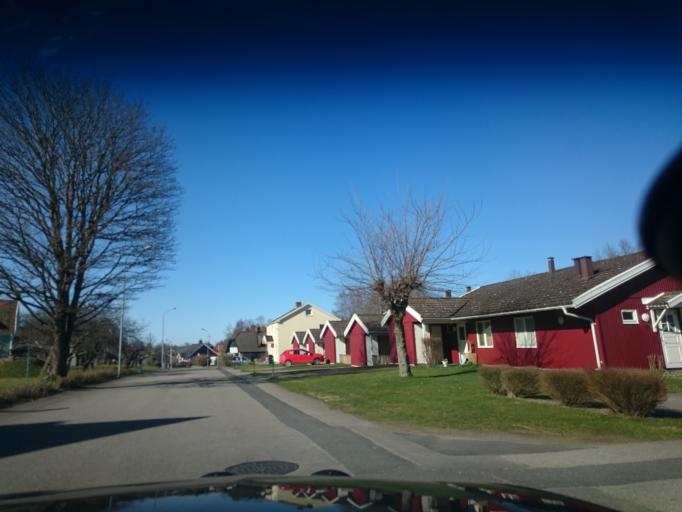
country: SE
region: Joenkoeping
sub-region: Vetlanda Kommun
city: Vetlanda
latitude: 57.3025
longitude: 15.1281
